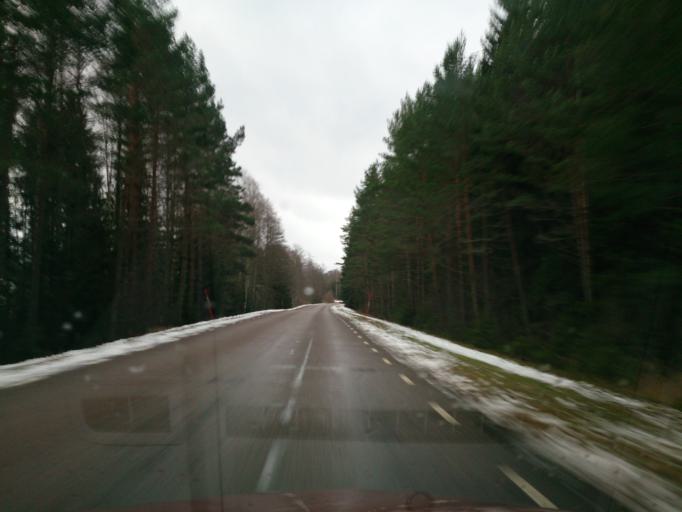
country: SE
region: OEstergoetland
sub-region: Atvidabergs Kommun
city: Atvidaberg
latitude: 58.2581
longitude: 16.0240
